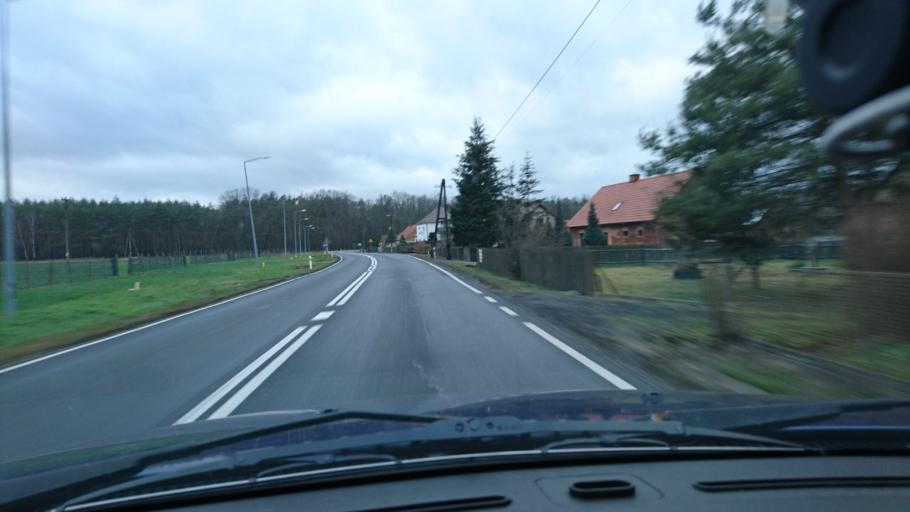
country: PL
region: Opole Voivodeship
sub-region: Powiat kluczborski
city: Kluczbork
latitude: 50.9465
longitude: 18.3181
